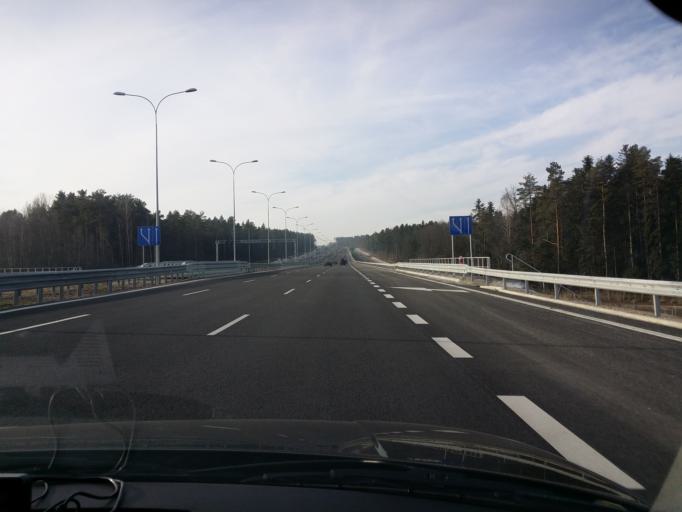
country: PL
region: Swietokrzyskie
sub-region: Powiat skarzyski
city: Skarzysko-Kamienna
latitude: 51.1562
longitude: 20.8496
